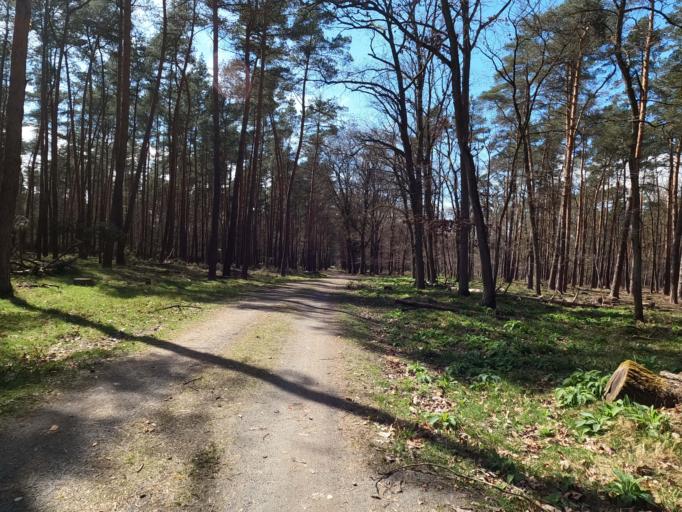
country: DE
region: Hesse
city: Raunheim
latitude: 50.0072
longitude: 8.5096
